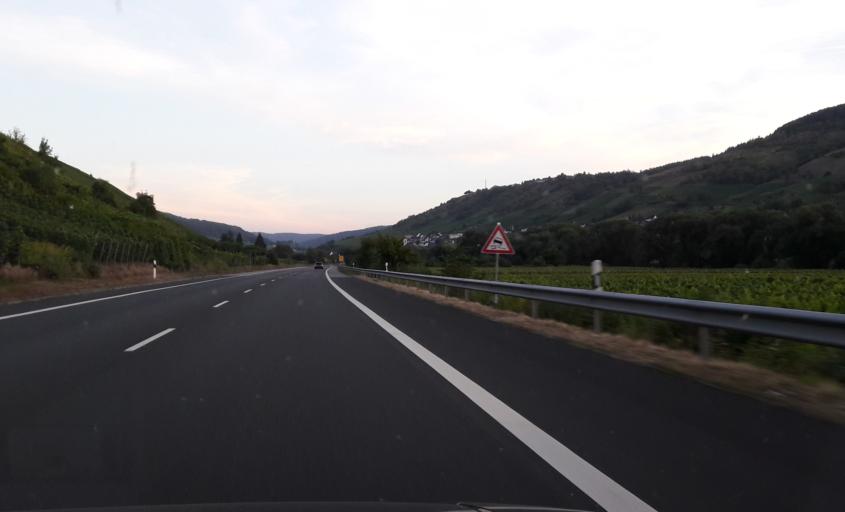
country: DE
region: Rheinland-Pfalz
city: Punderich
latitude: 50.0303
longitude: 7.1183
